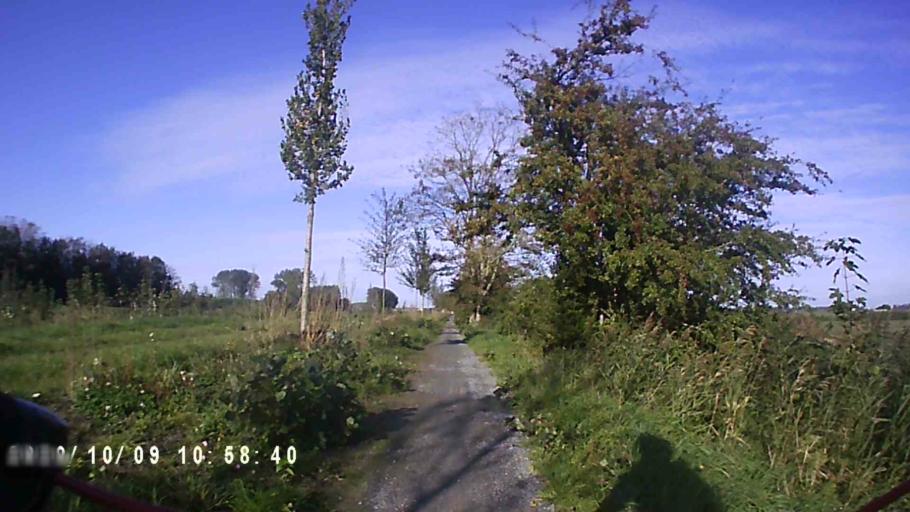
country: NL
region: Groningen
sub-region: Gemeente Groningen
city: Korrewegwijk
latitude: 53.2553
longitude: 6.5164
